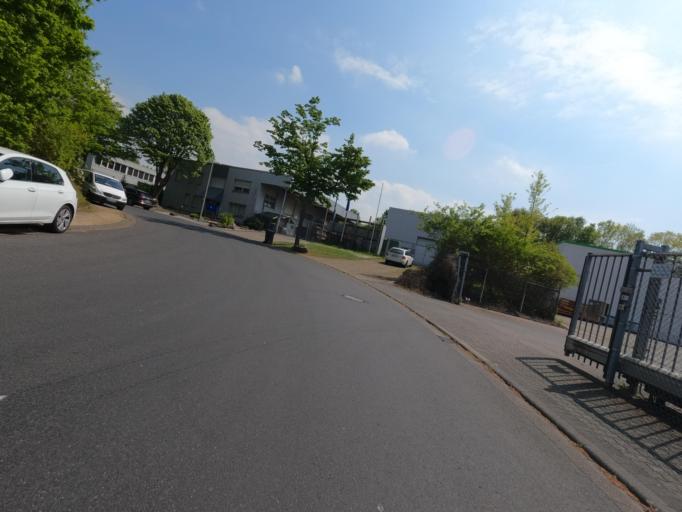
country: DE
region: North Rhine-Westphalia
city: Baesweiler
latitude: 50.9151
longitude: 6.1703
